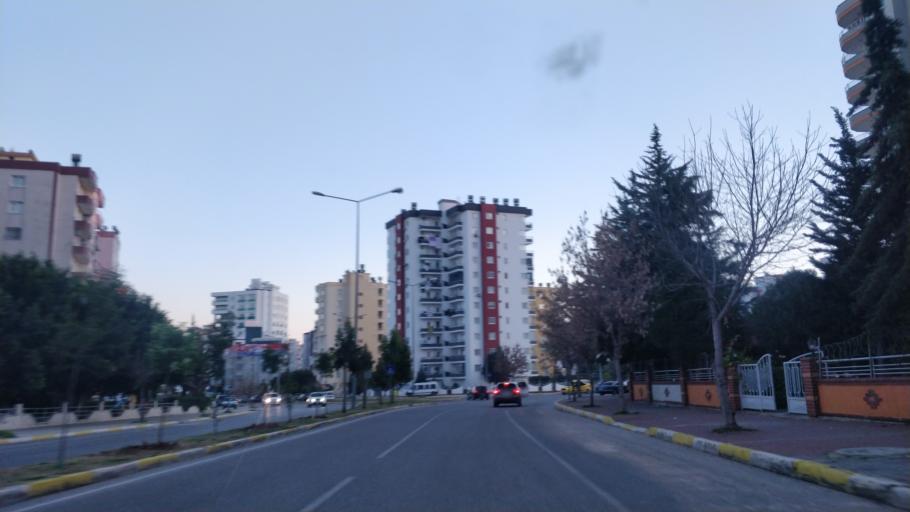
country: TR
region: Mersin
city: Mercin
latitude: 36.7929
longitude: 34.5881
